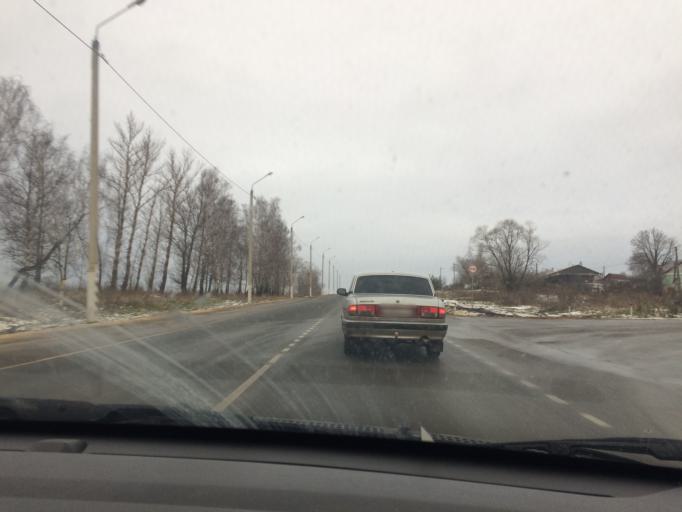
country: RU
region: Tula
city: Gorelki
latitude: 54.2385
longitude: 37.6591
